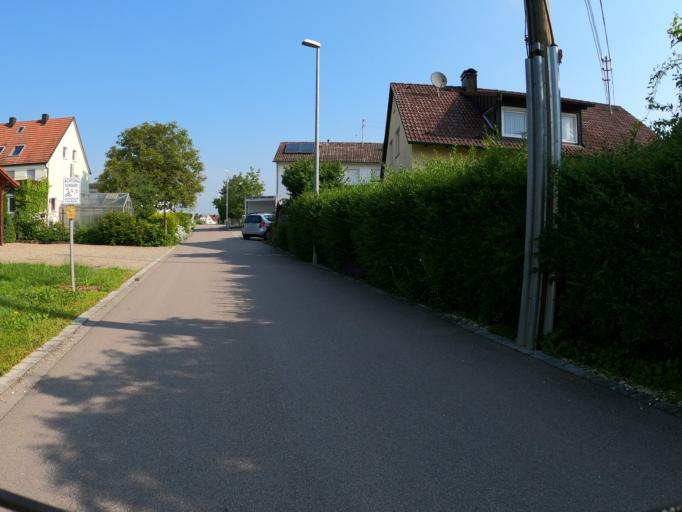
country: DE
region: Bavaria
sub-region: Swabia
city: Pfaffenhofen an der Roth
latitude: 48.3521
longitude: 10.1559
